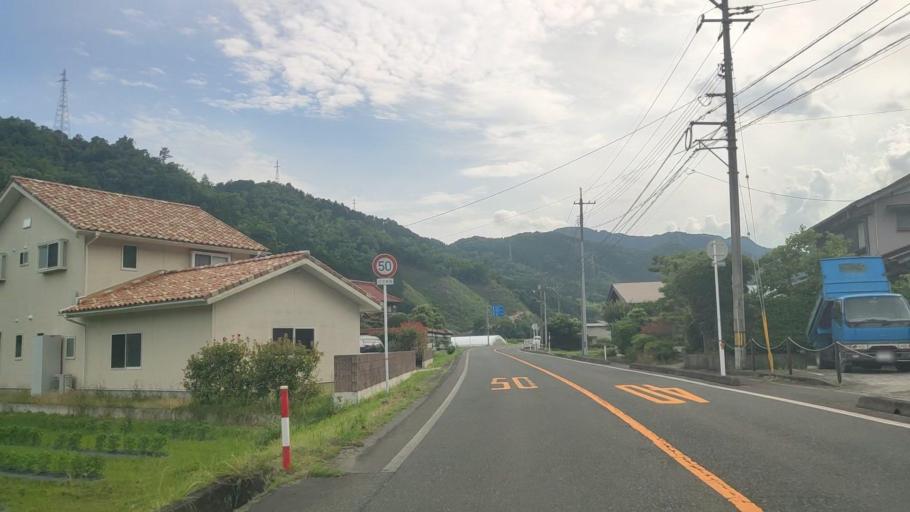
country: JP
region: Tottori
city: Tottori
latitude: 35.3410
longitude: 134.1959
